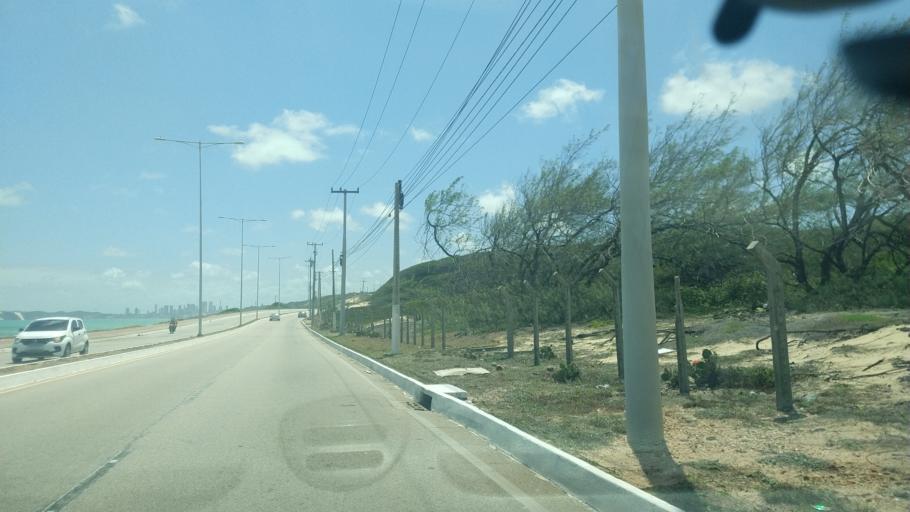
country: BR
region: Rio Grande do Norte
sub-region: Natal
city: Natal
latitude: -5.8127
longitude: -35.1821
